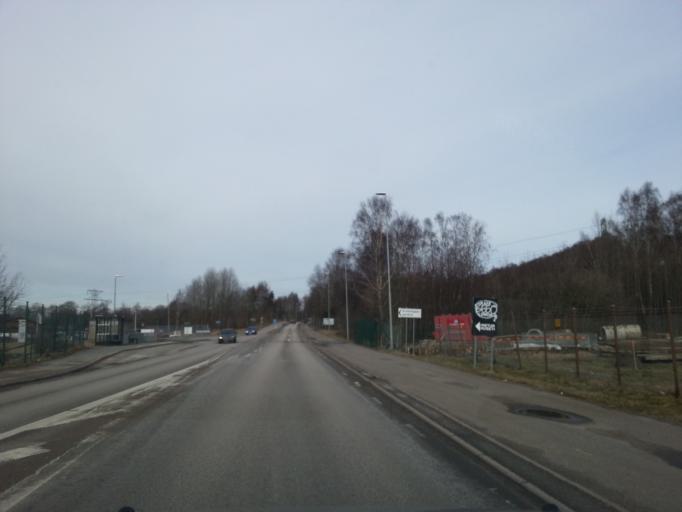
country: SE
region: Vaestra Goetaland
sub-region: Goteborg
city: Eriksbo
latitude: 57.7565
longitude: 12.0108
